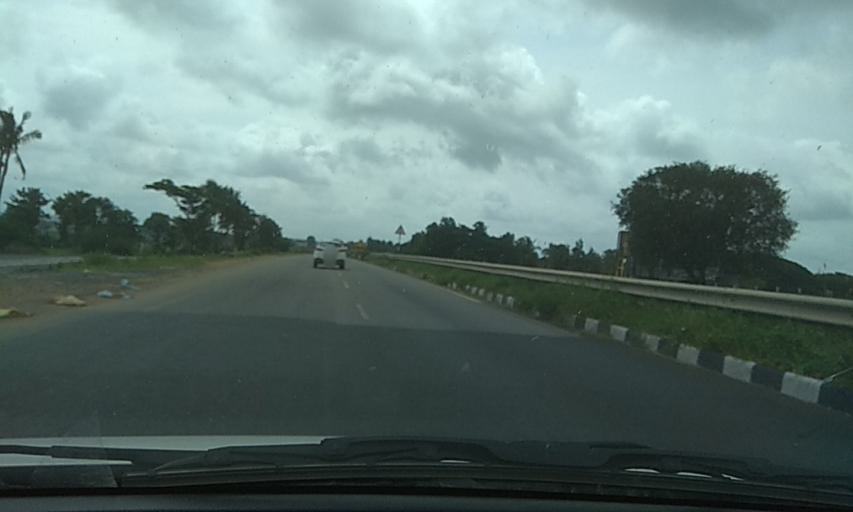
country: IN
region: Karnataka
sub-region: Davanagere
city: Harihar
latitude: 14.4596
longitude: 75.8577
